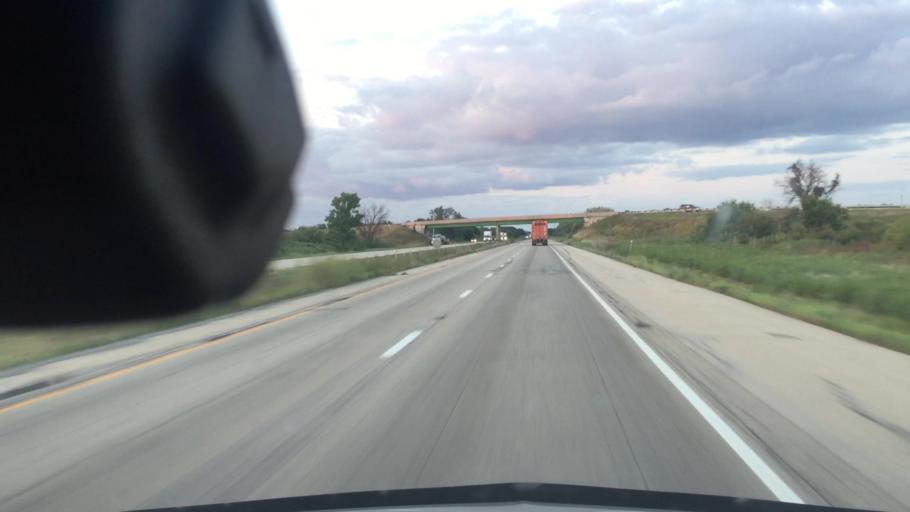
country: US
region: Illinois
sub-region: Grundy County
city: Gardner
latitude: 41.2044
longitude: -88.3042
